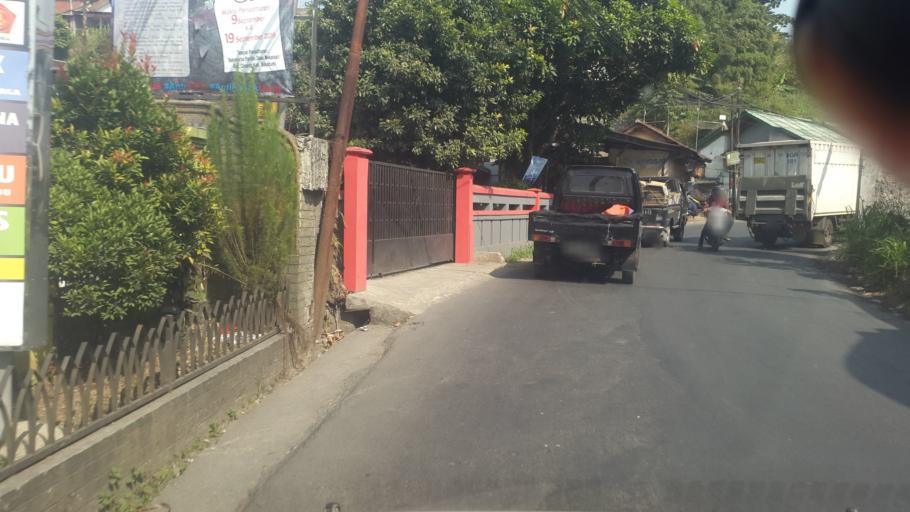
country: ID
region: West Java
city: Cicurug
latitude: -6.7964
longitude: 106.7726
